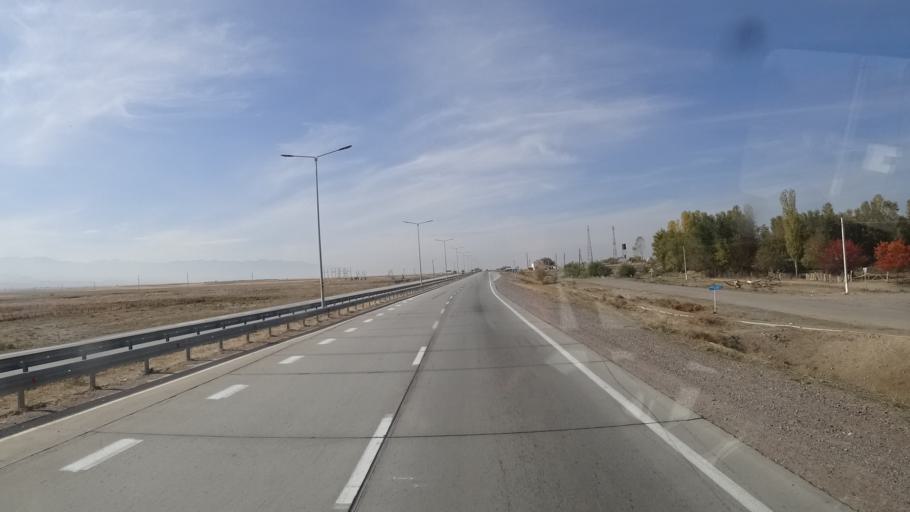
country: KZ
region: Zhambyl
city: Merke
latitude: 42.8888
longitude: 72.9917
